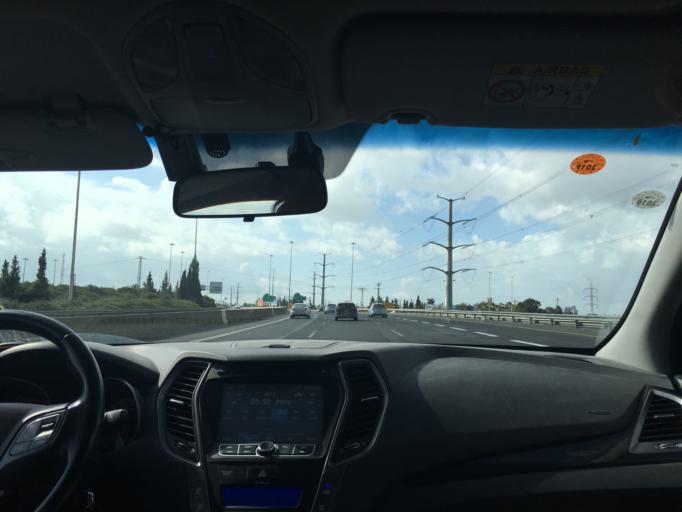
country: IL
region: Tel Aviv
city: Azor
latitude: 32.0128
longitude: 34.8162
